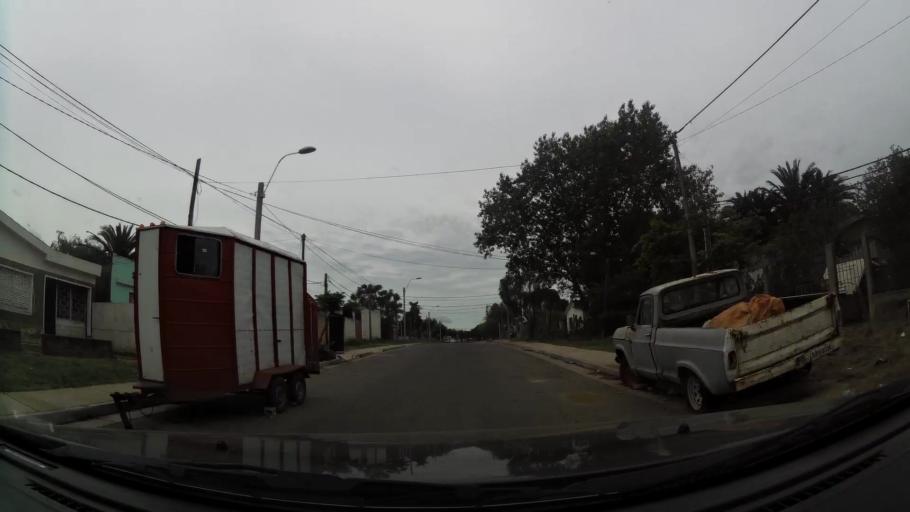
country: UY
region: Canelones
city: Las Piedras
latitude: -34.7304
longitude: -56.2079
